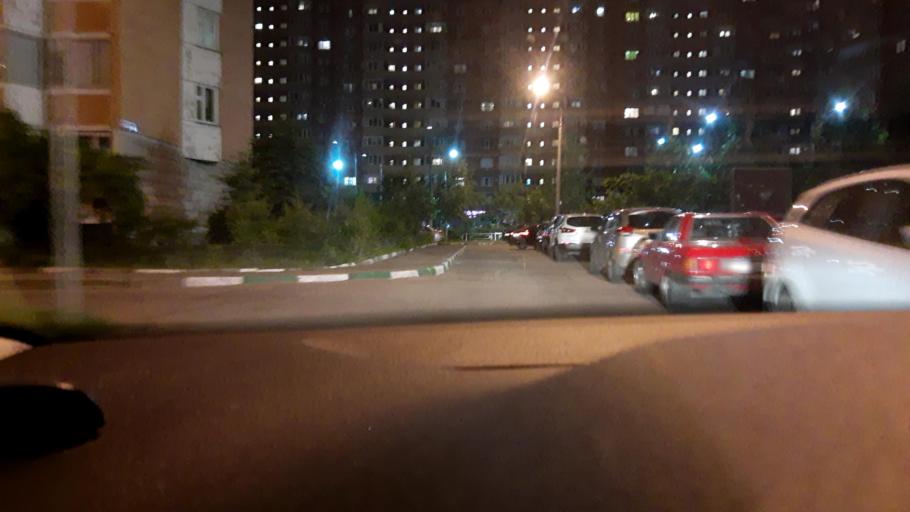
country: RU
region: Moskovskaya
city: Krasnogorsk
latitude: 55.8313
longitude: 37.2944
